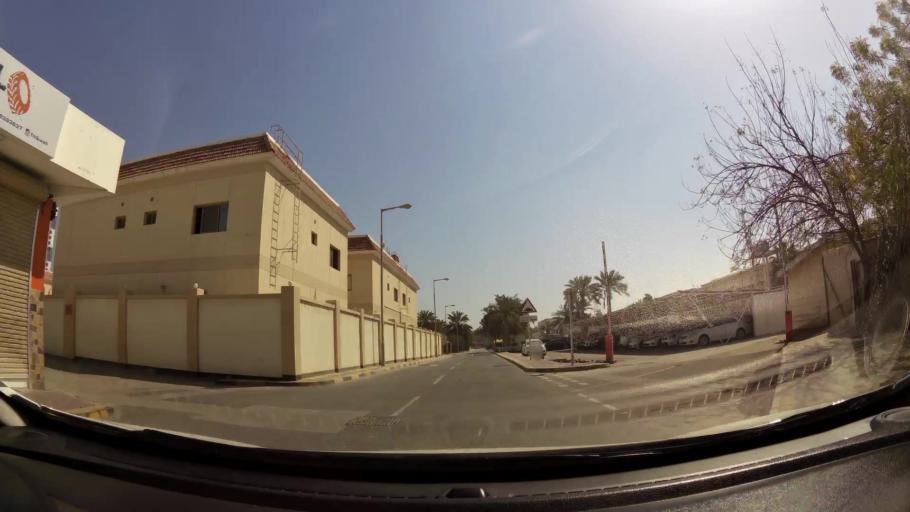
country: BH
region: Manama
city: Manama
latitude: 26.2098
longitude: 50.6048
